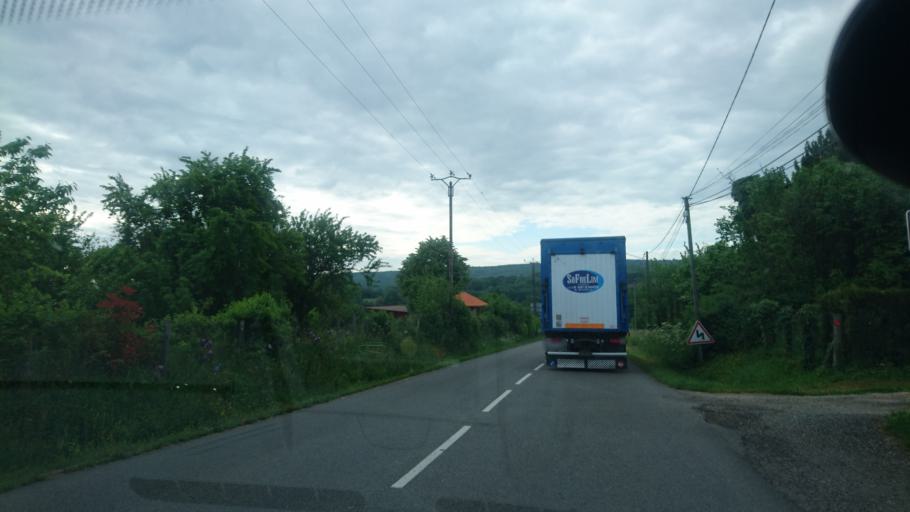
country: FR
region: Limousin
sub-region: Departement de la Haute-Vienne
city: Chateauneuf-la-Foret
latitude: 45.7056
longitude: 1.5889
